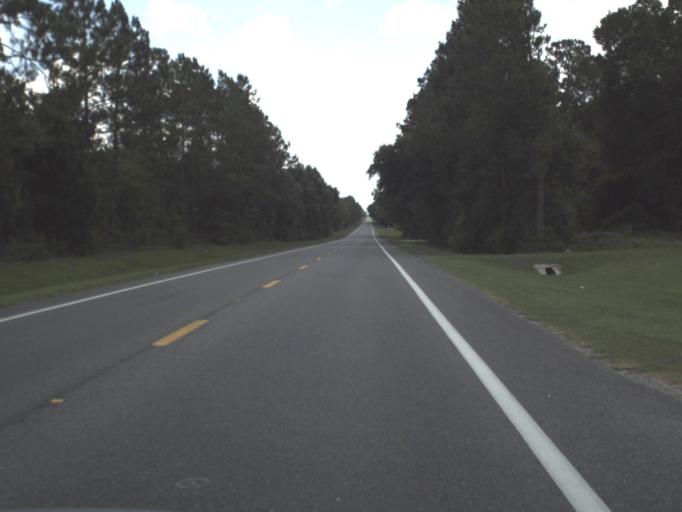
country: US
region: Florida
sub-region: Union County
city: Lake Butler
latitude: 29.9828
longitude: -82.3916
